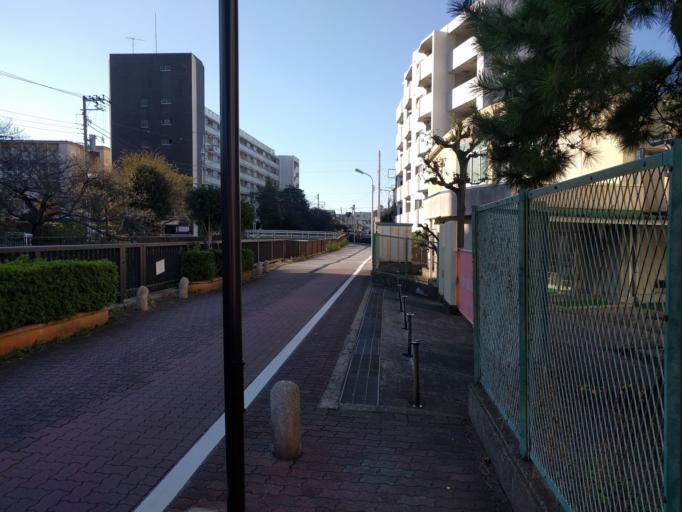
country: JP
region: Kanagawa
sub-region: Kawasaki-shi
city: Kawasaki
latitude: 35.5733
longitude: 139.7131
